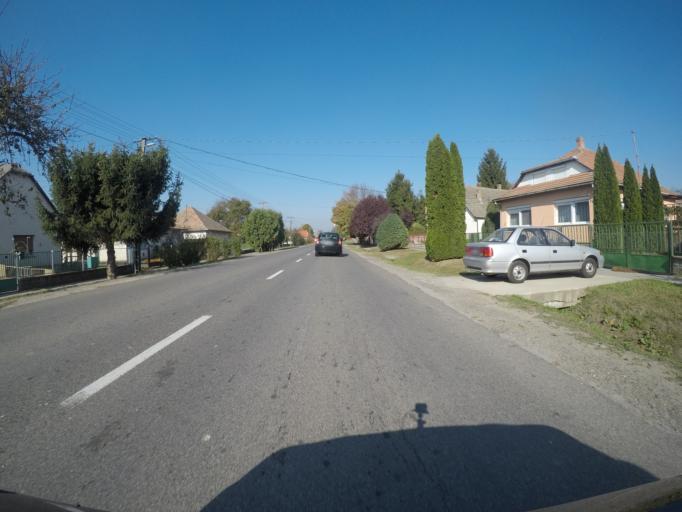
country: HU
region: Tolna
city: Szedres
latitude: 46.4714
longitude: 18.6854
